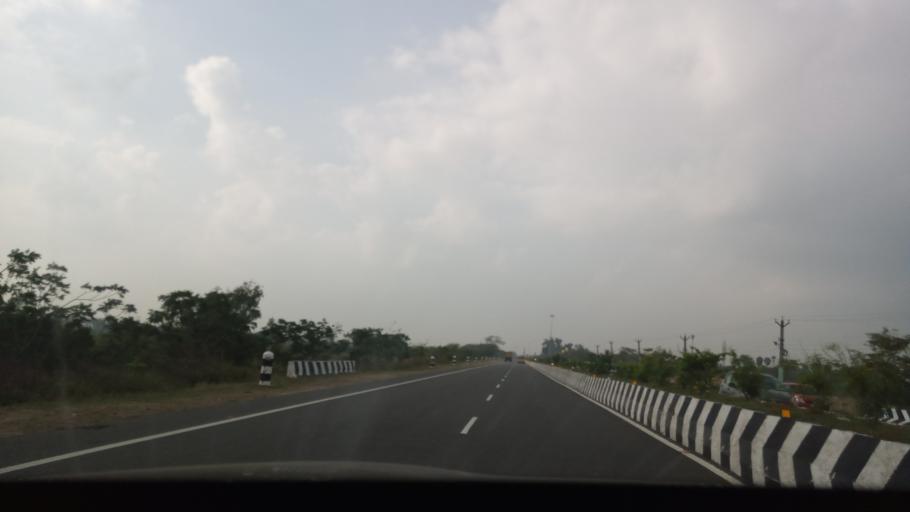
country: IN
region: Tamil Nadu
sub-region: Kancheepuram
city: Injambakkam
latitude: 12.7671
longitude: 80.2469
